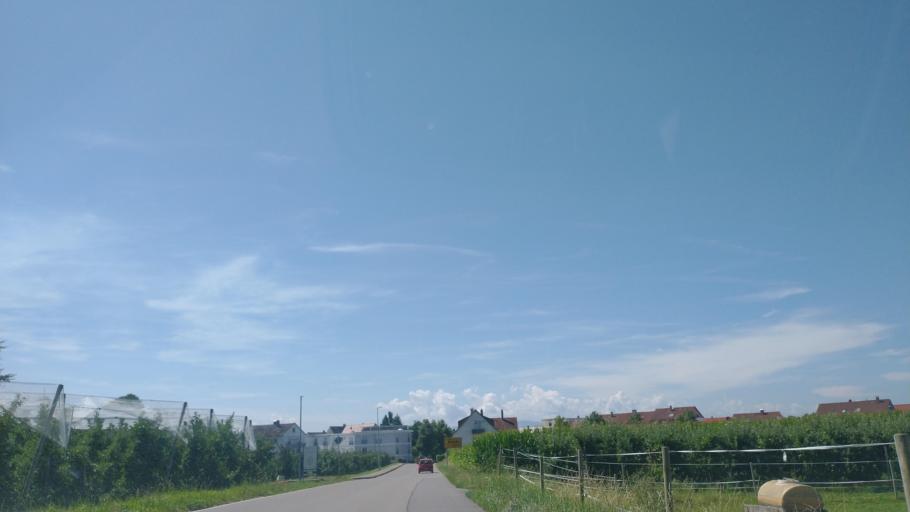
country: DE
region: Baden-Wuerttemberg
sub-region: Tuebingen Region
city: Kressbronn am Bodensee
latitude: 47.6005
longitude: 9.5977
